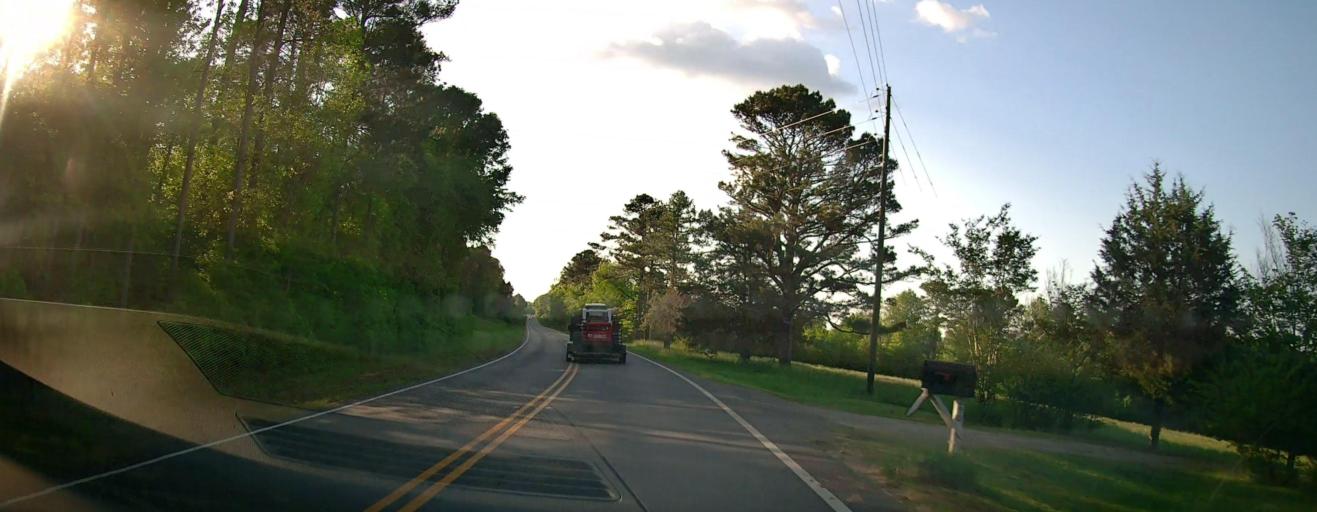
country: US
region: Georgia
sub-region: Putnam County
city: Eatonton
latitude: 33.3256
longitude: -83.4986
